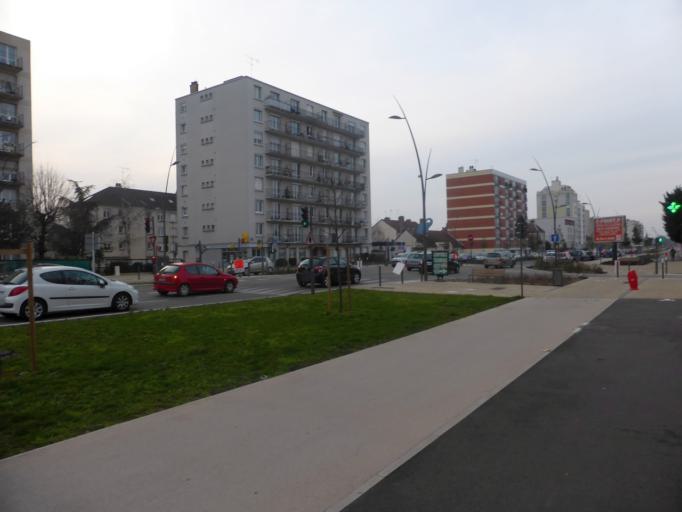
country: FR
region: Champagne-Ardenne
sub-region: Departement de l'Aube
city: Troyes
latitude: 48.3032
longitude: 4.0734
